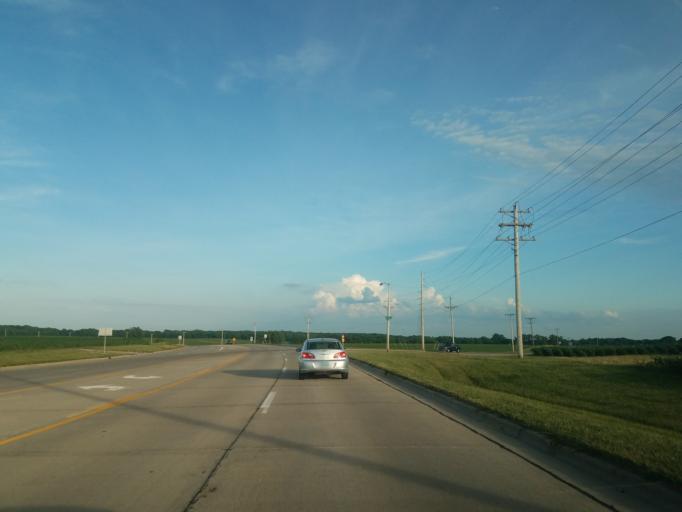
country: US
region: Illinois
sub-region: McLean County
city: Bloomington
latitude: 40.4504
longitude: -88.9662
